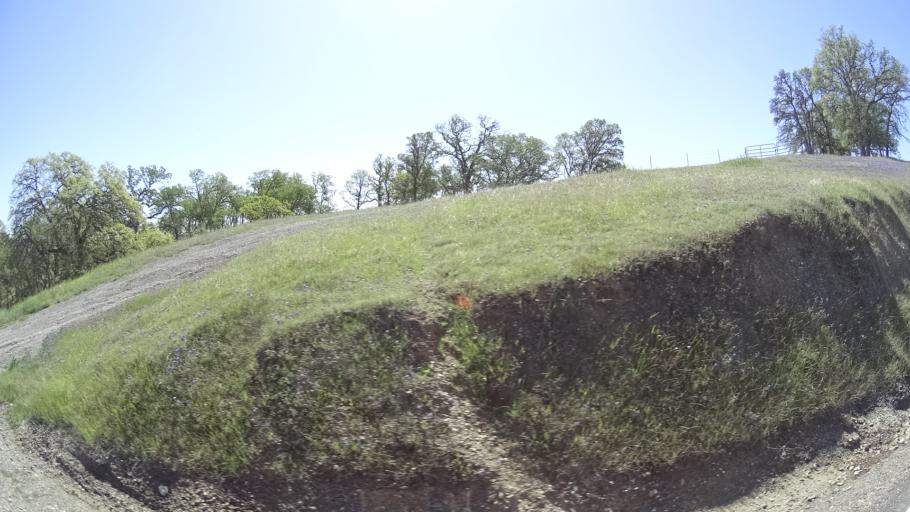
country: US
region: California
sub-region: Tehama County
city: Rancho Tehama Reserve
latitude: 39.8164
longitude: -122.3864
